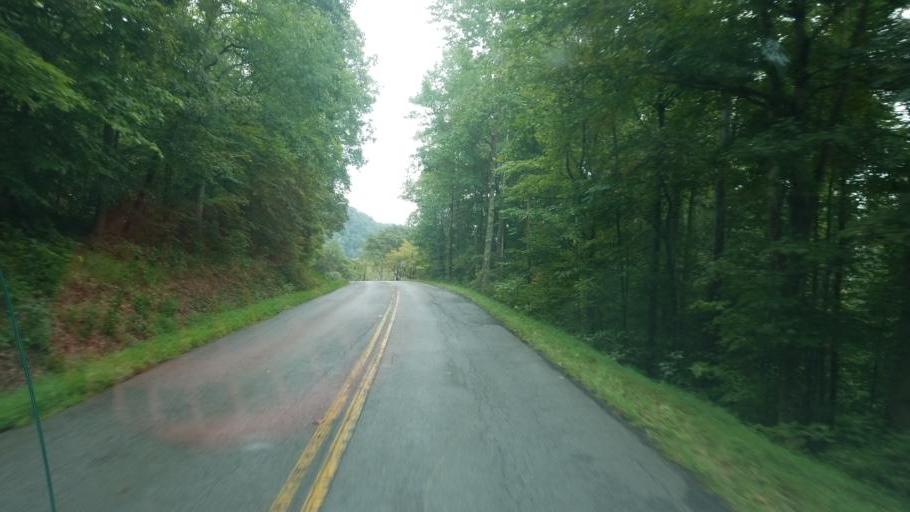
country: US
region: Kentucky
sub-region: Rowan County
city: Morehead
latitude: 38.3551
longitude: -83.5309
